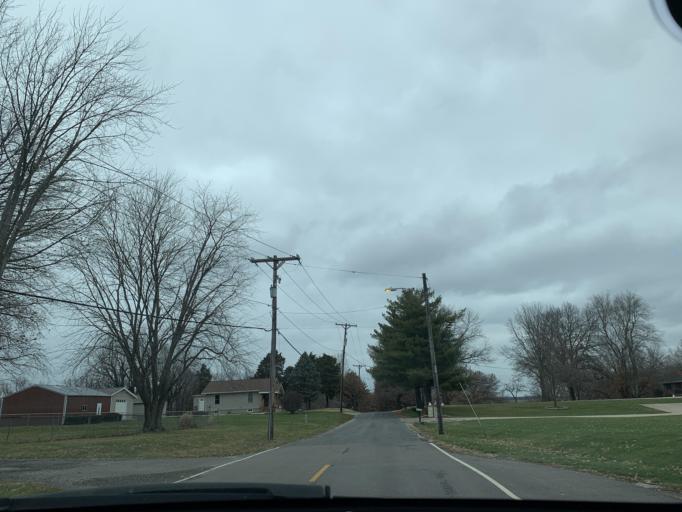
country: US
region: Illinois
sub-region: Sangamon County
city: Springfield
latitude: 39.8279
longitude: -89.6875
